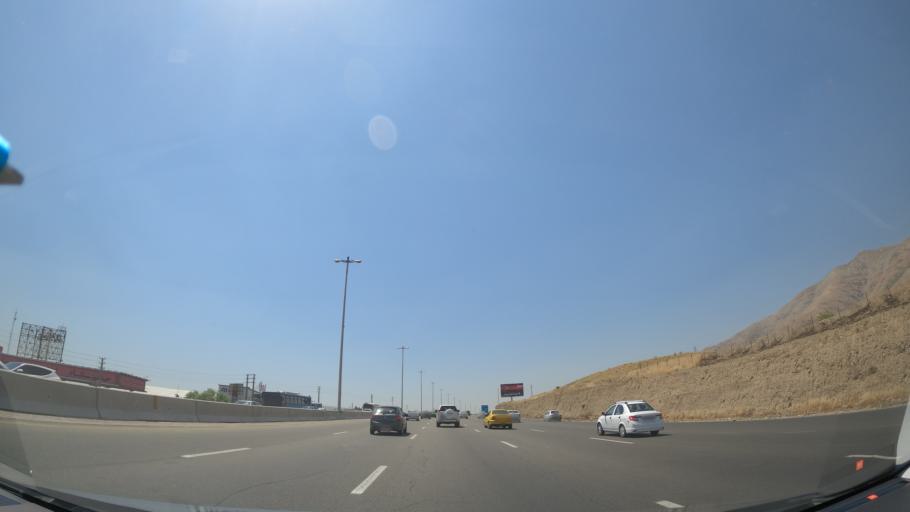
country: IR
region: Tehran
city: Shahr-e Qods
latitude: 35.7465
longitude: 51.0881
